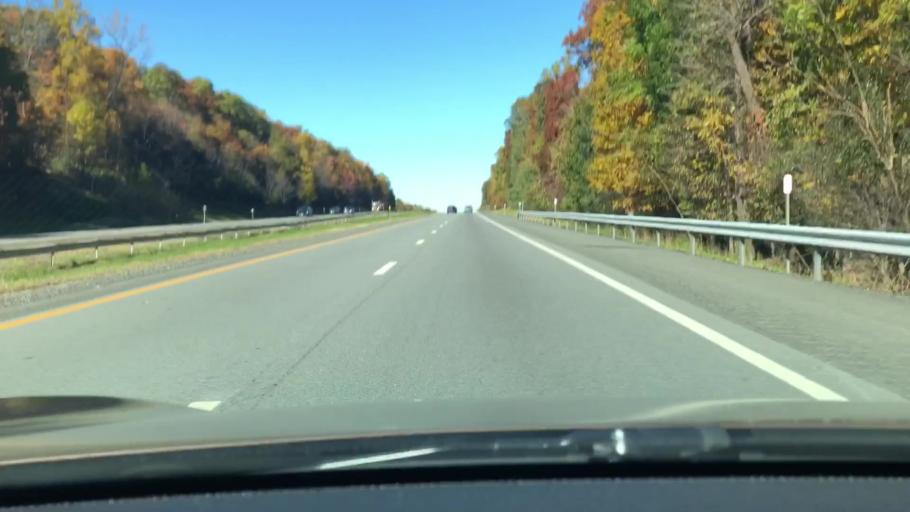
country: US
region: New York
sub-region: Orange County
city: Vails Gate
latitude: 41.4595
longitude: -74.0663
